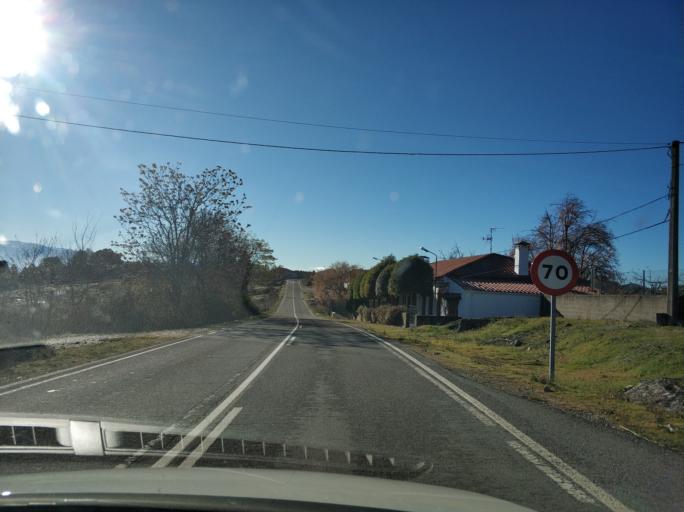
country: ES
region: Castille and Leon
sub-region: Provincia de Salamanca
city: San Miguel de Valero
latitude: 40.5468
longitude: -5.9192
